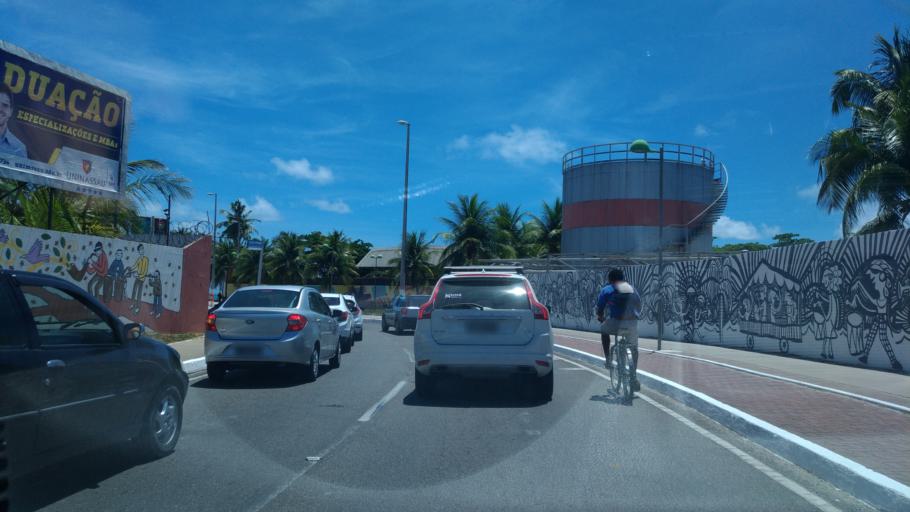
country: BR
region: Alagoas
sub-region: Maceio
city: Maceio
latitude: -9.6747
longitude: -35.7184
